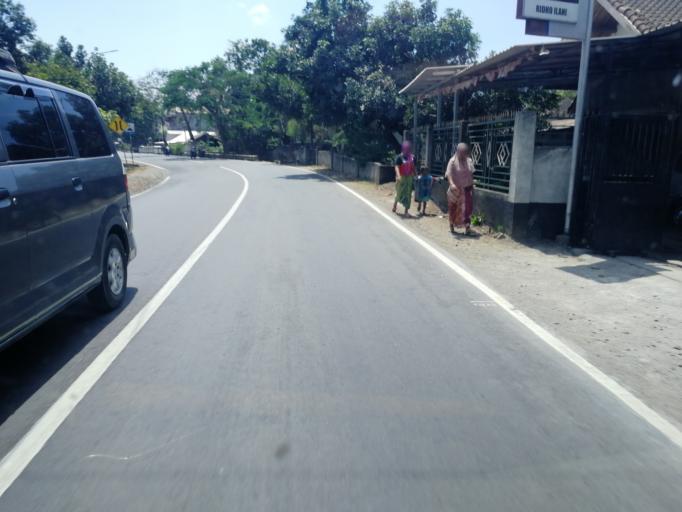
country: ID
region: West Nusa Tenggara
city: Jelateng Timur
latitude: -8.7074
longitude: 116.0829
